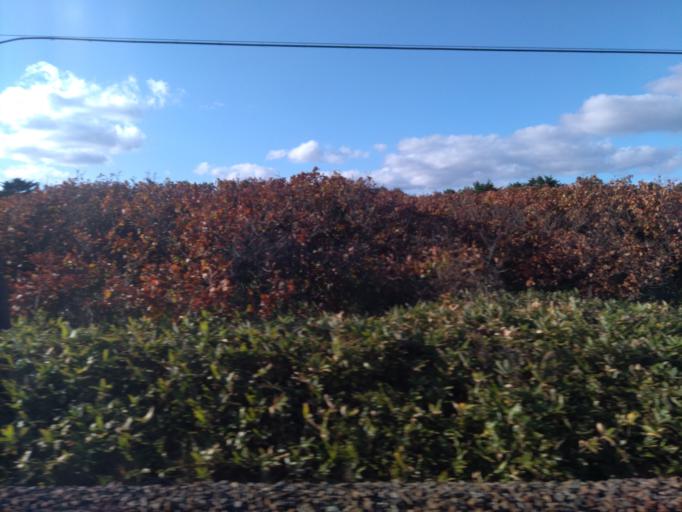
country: JP
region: Hokkaido
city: Niseko Town
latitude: 42.5515
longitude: 140.4190
